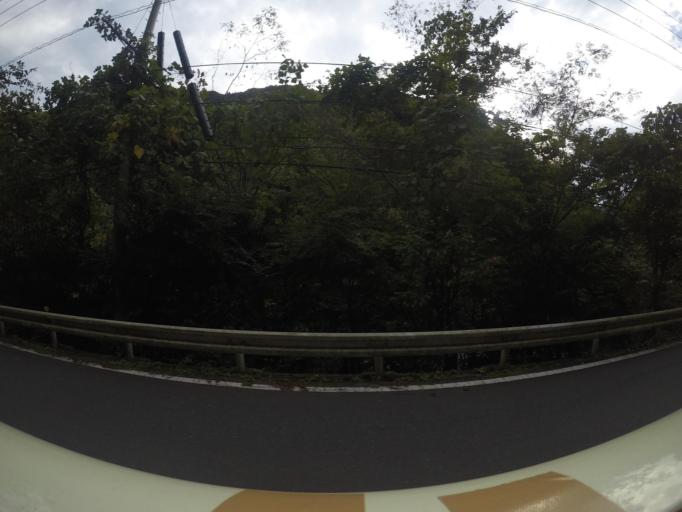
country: JP
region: Gunma
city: Yoshii
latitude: 36.1287
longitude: 138.9506
